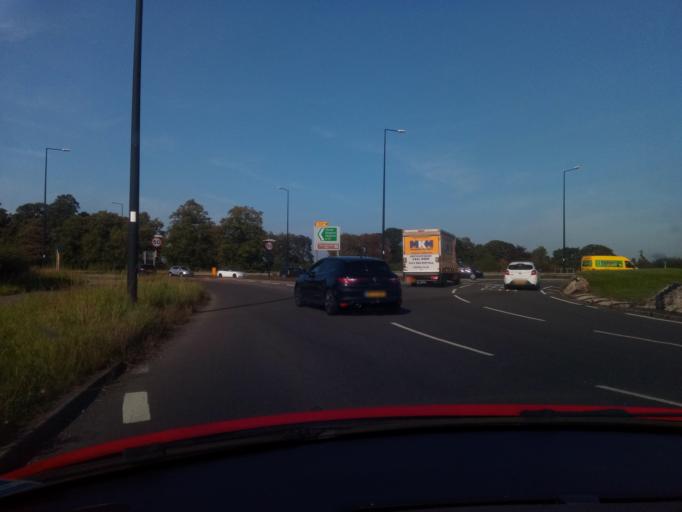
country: GB
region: England
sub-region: City of York
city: Skelton
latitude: 54.0064
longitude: -1.1411
